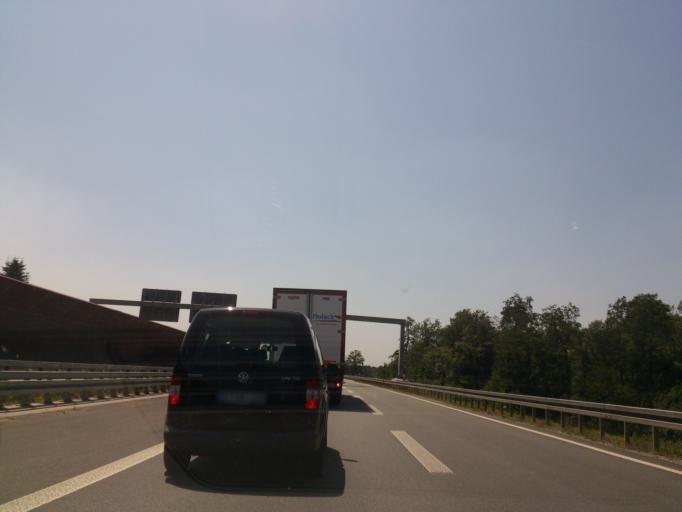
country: DE
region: North Rhine-Westphalia
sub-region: Regierungsbezirk Detmold
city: Bielefeld
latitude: 51.9791
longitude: 8.4846
